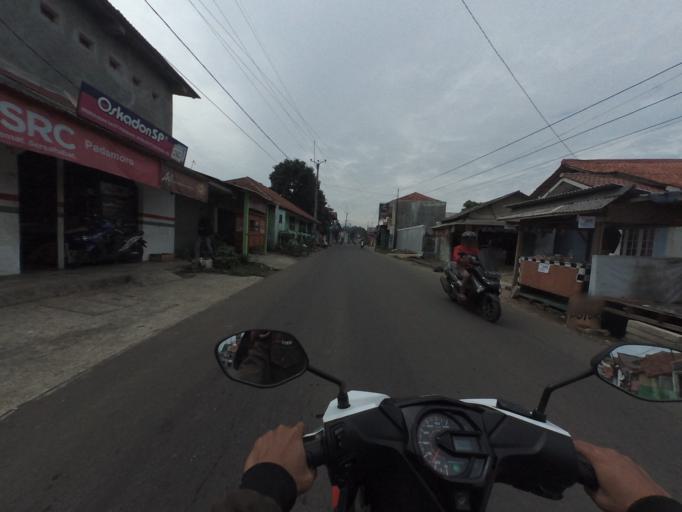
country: ID
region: West Java
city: Ciampea
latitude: -6.5939
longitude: 106.6530
